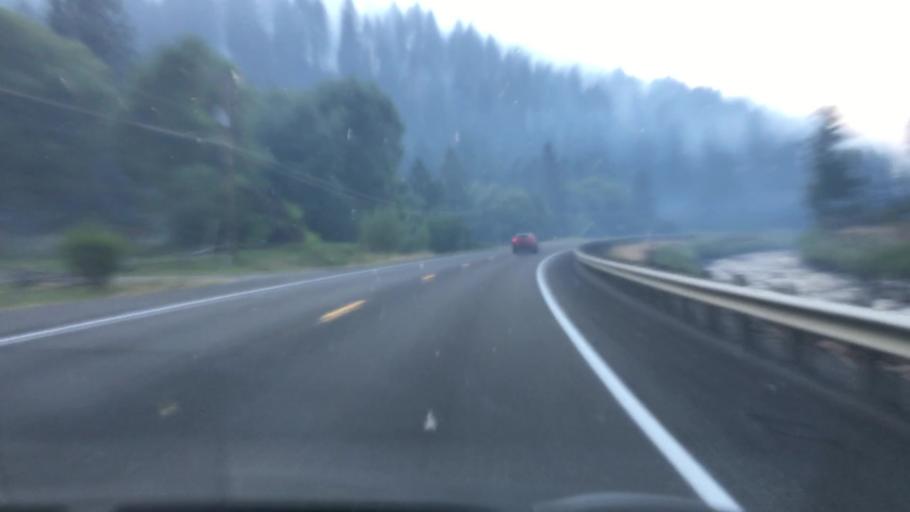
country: US
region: Idaho
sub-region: Valley County
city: McCall
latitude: 45.2387
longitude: -116.3303
